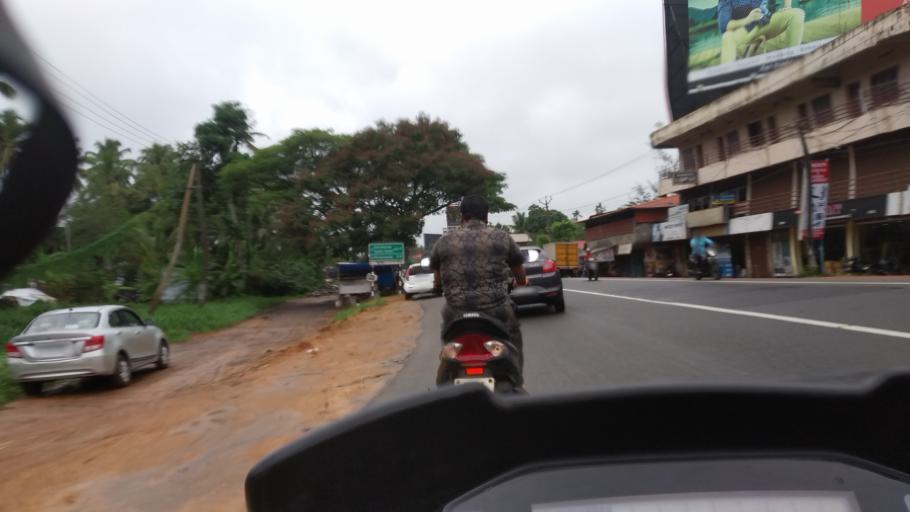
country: IN
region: Kerala
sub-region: Alappuzha
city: Mavelikara
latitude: 9.2813
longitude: 76.4571
